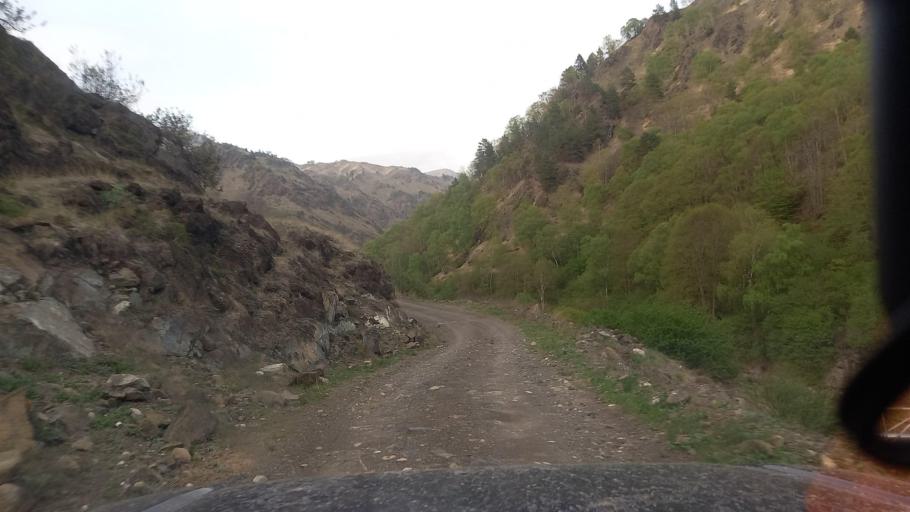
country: RU
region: Kabardino-Balkariya
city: Kamennomostskoye
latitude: 43.7200
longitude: 42.8431
